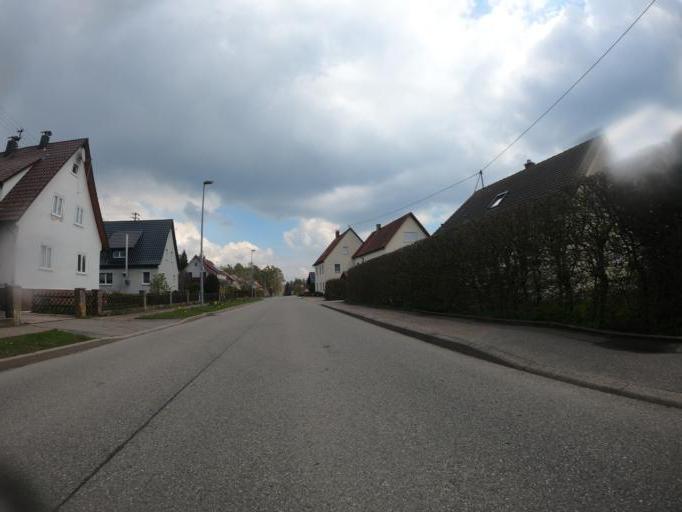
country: DE
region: Baden-Wuerttemberg
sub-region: Karlsruhe Region
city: Oberreichenbach
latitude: 48.7465
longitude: 8.6873
